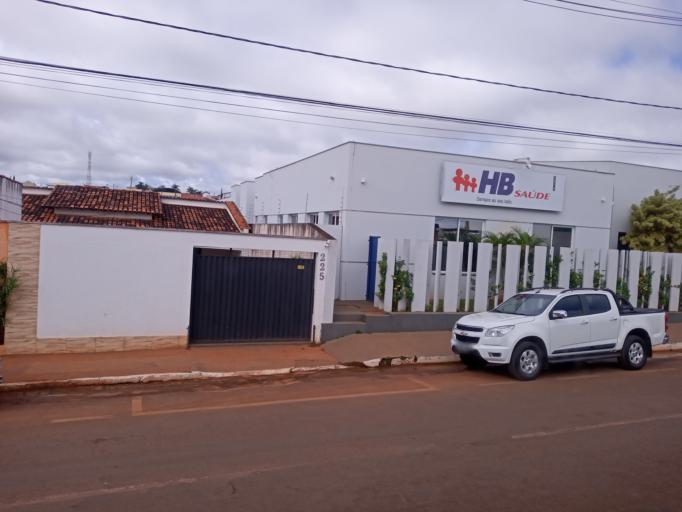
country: BR
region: Minas Gerais
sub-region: Sacramento
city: Sacramento
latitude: -19.3111
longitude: -47.5313
